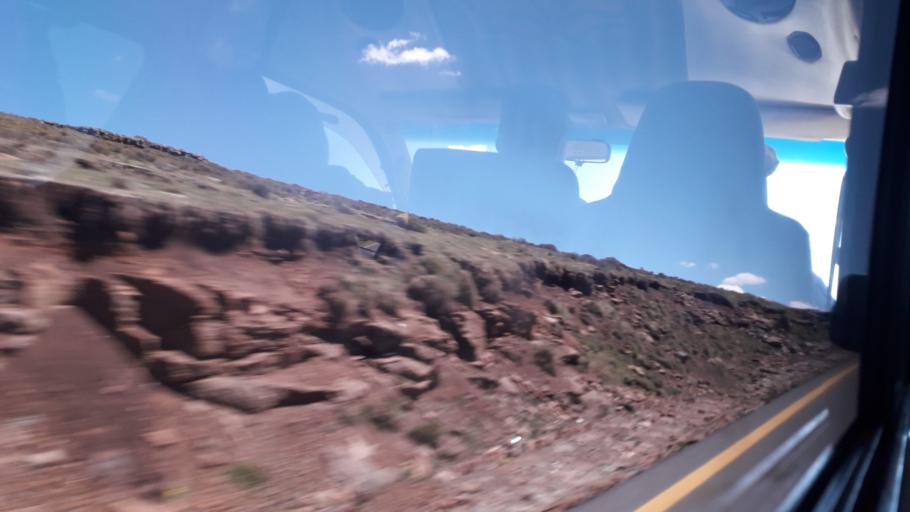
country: LS
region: Mokhotlong
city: Mokhotlong
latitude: -29.0606
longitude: 28.8513
